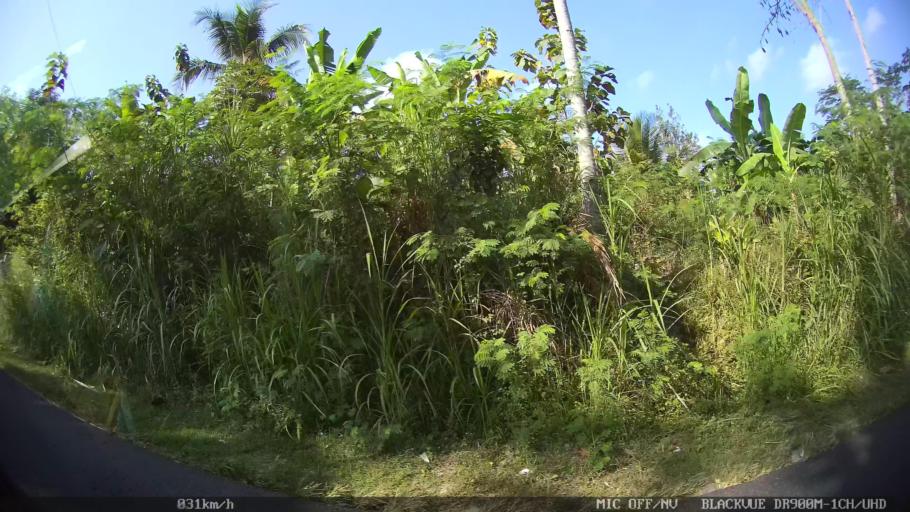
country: ID
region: Daerah Istimewa Yogyakarta
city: Kasihan
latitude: -7.8345
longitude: 110.2765
